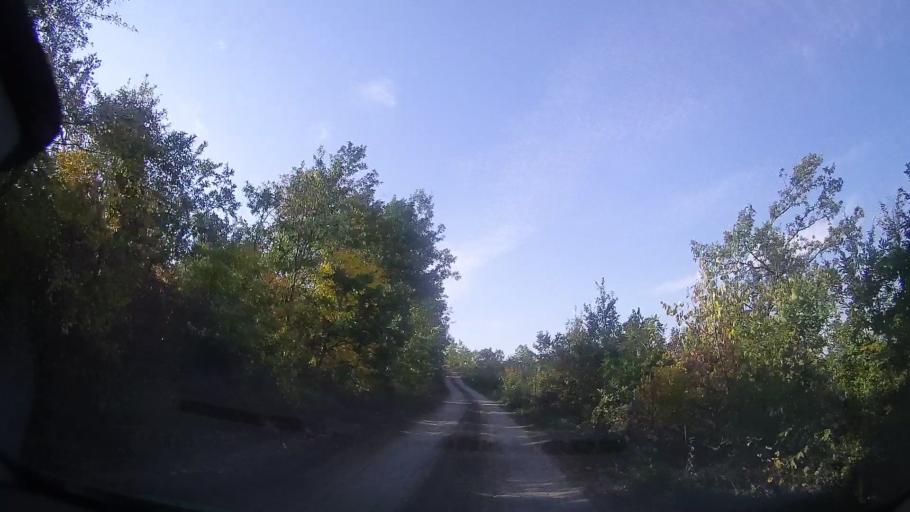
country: RO
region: Timis
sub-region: Comuna Bogda
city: Bogda
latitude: 45.9213
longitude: 21.6127
